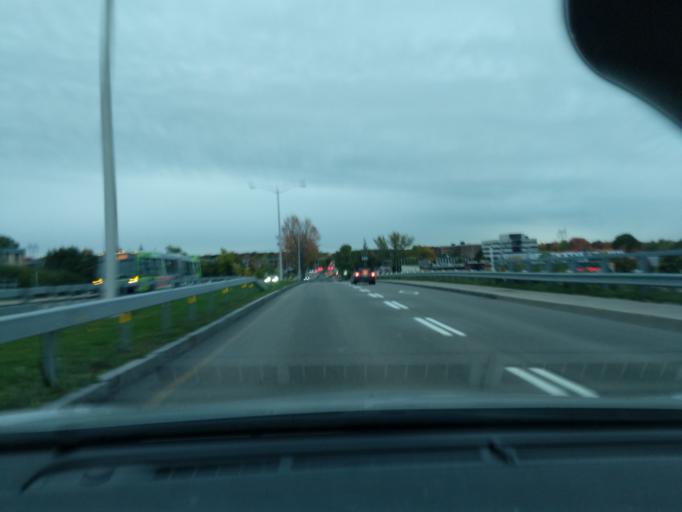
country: CA
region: Quebec
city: L'Ancienne-Lorette
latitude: 46.7653
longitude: -71.3135
